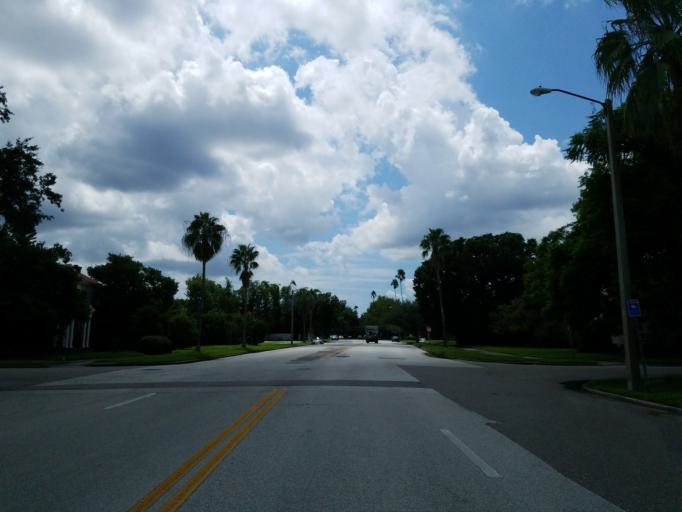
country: US
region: Florida
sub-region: Hillsborough County
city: Tampa
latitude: 27.9291
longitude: -82.4571
